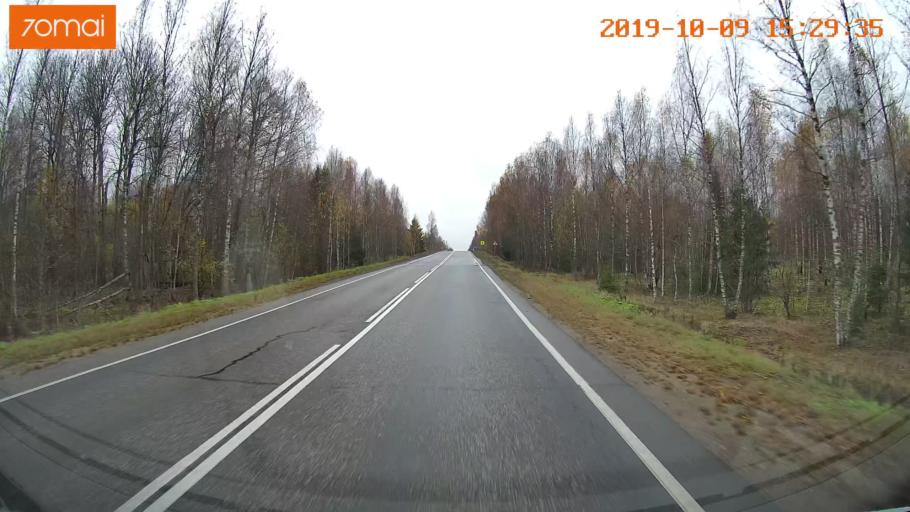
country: RU
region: Kostroma
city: Susanino
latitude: 57.9897
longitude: 41.3402
